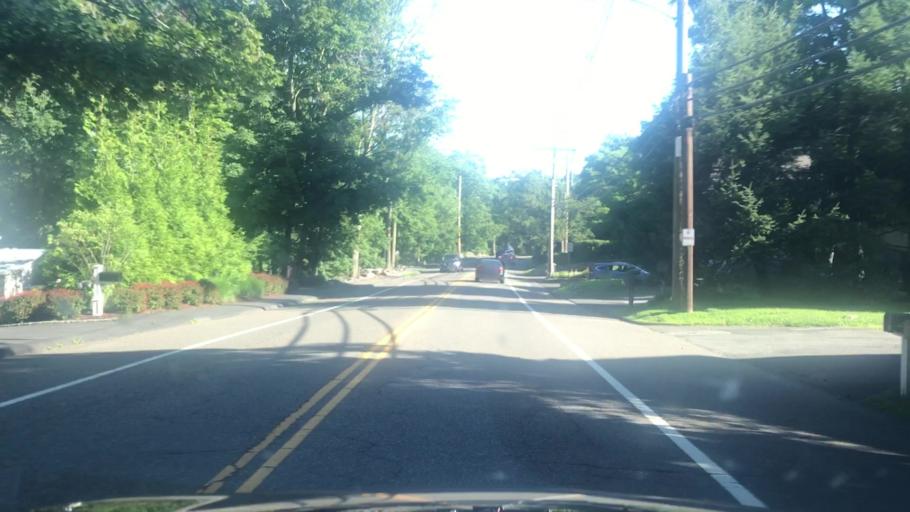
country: US
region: Connecticut
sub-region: Fairfield County
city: Pemberwick
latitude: 41.0203
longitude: -73.6500
